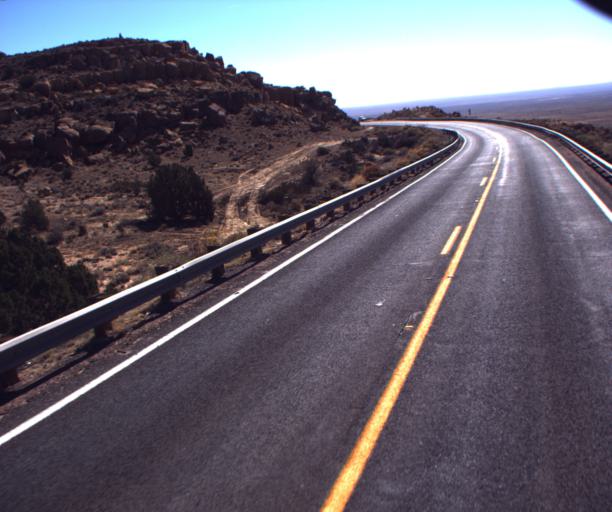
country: US
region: Arizona
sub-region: Navajo County
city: First Mesa
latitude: 35.8972
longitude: -110.6642
